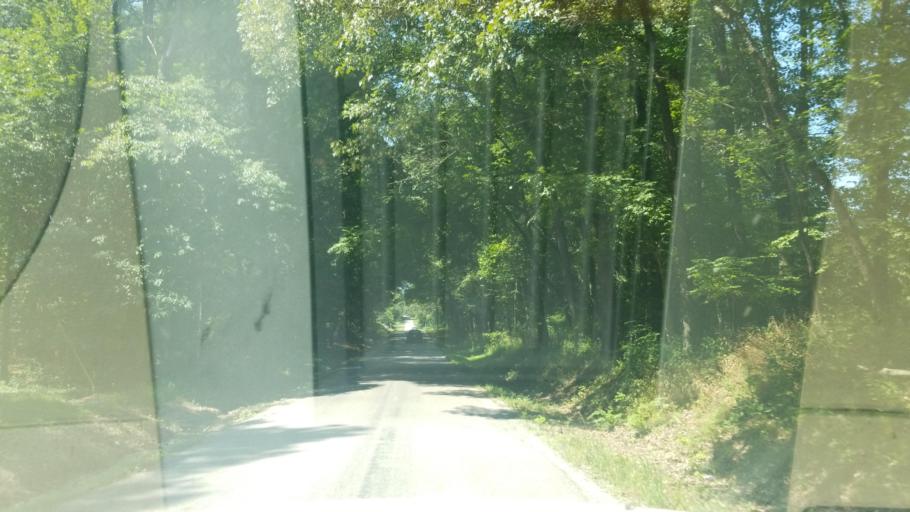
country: US
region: Illinois
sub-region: Saline County
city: Carrier Mills
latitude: 37.7941
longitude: -88.6386
